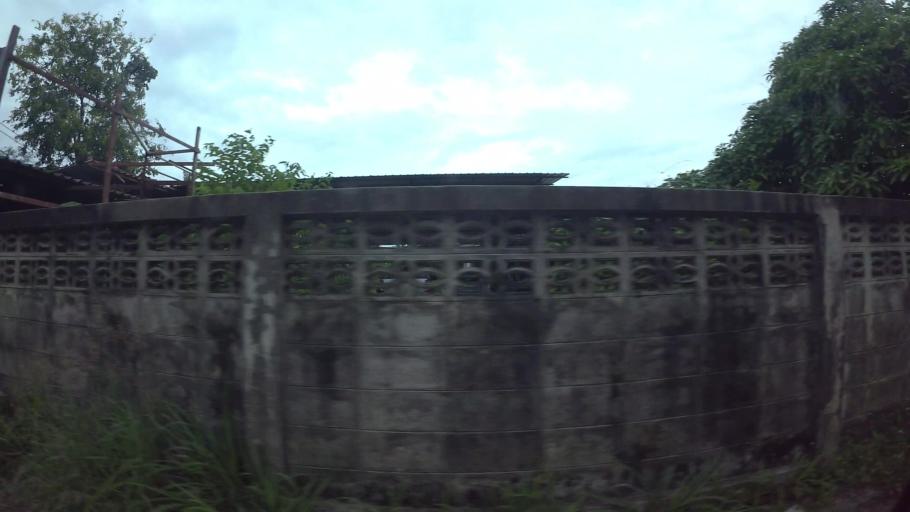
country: TH
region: Chon Buri
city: Sattahip
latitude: 12.6957
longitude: 100.8997
